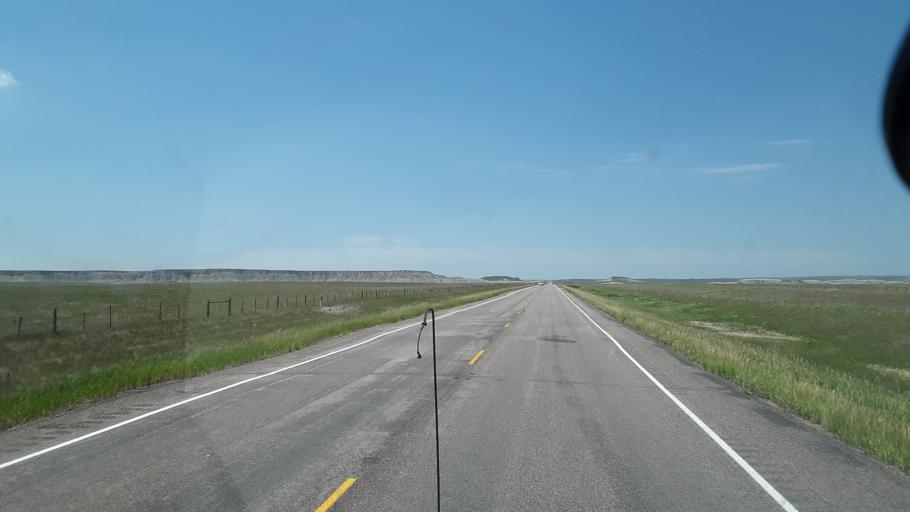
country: US
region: South Dakota
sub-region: Shannon County
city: Porcupine
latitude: 43.7174
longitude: -102.2836
